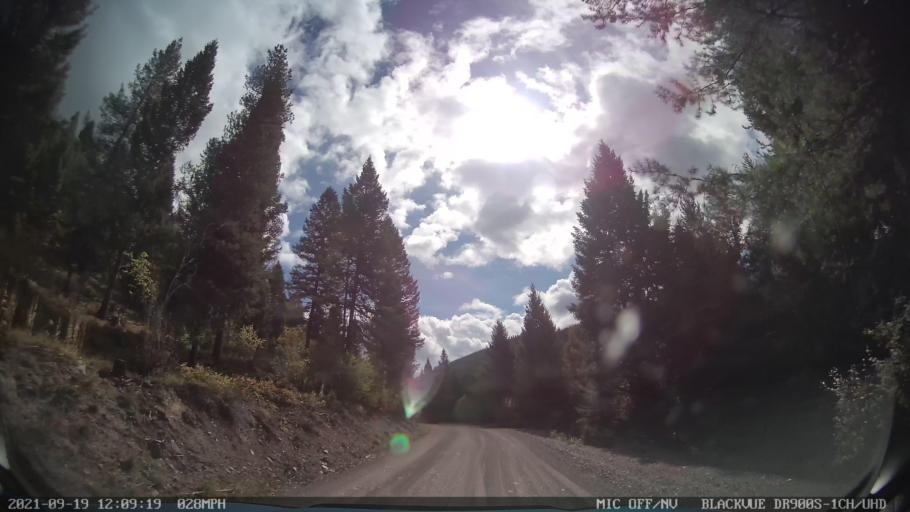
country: US
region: Montana
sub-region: Missoula County
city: Seeley Lake
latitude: 47.1841
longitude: -113.3919
